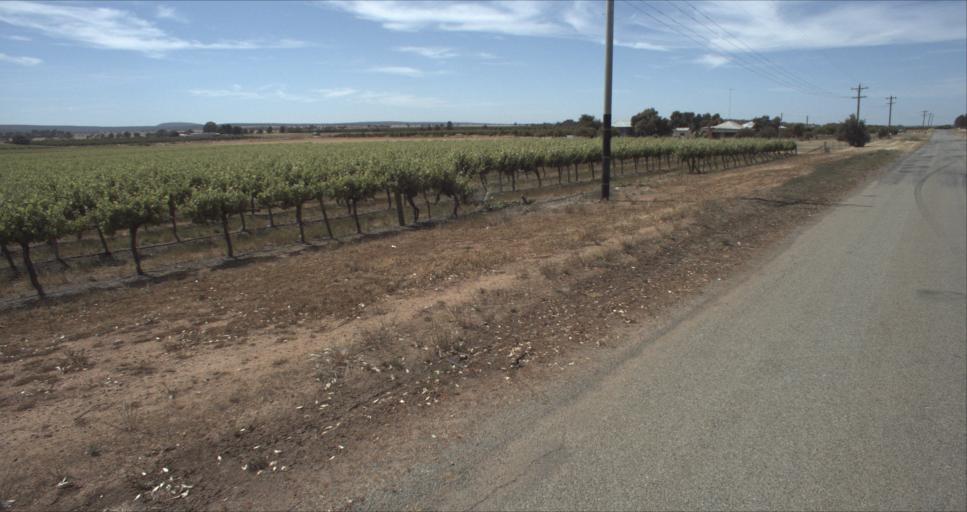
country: AU
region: New South Wales
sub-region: Leeton
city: Leeton
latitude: -34.5642
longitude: 146.4619
